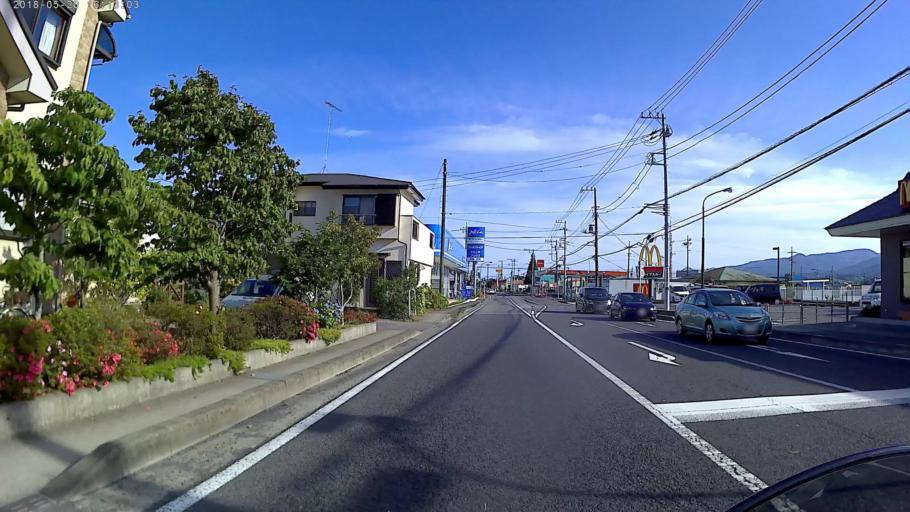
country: JP
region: Kanagawa
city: Odawara
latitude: 35.3208
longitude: 139.1590
